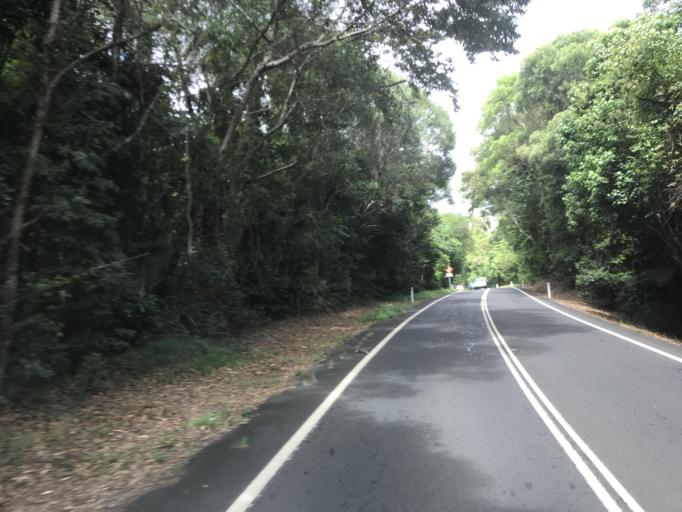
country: AU
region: Queensland
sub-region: Cassowary Coast
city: Innisfail
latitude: -17.8657
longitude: 146.0777
